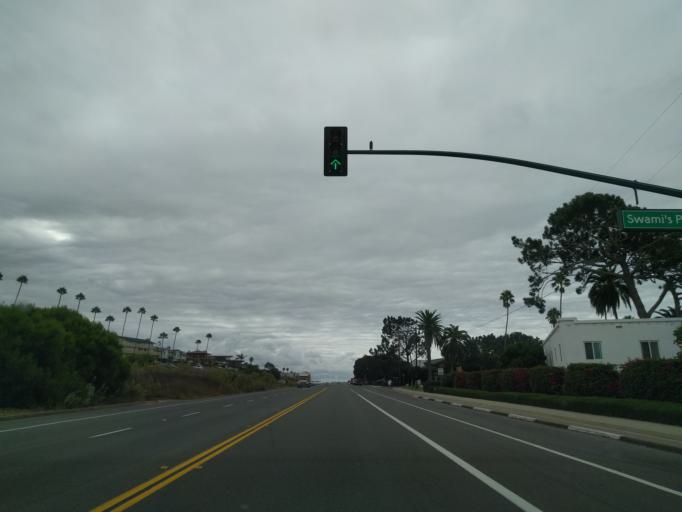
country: US
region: California
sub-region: San Diego County
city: Encinitas
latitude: 33.0357
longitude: -117.2918
